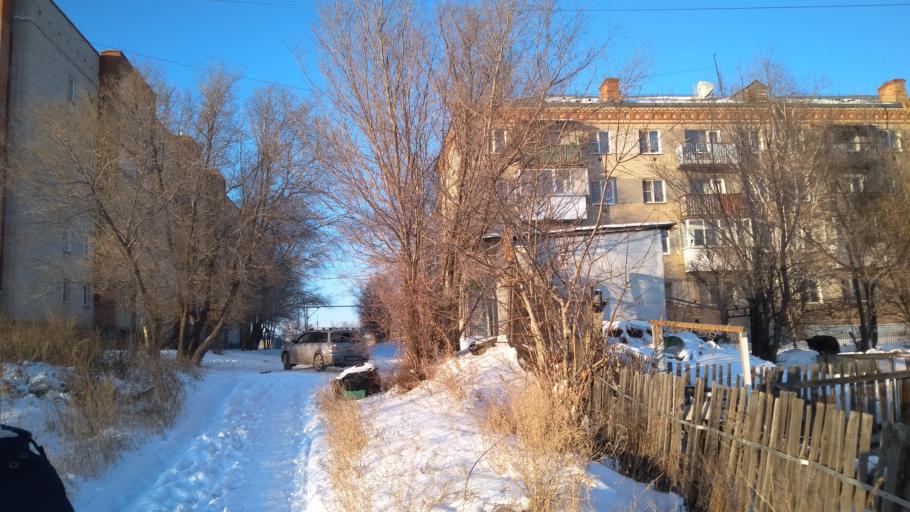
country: RU
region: Chelyabinsk
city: Troitsk
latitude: 54.0839
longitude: 61.5755
